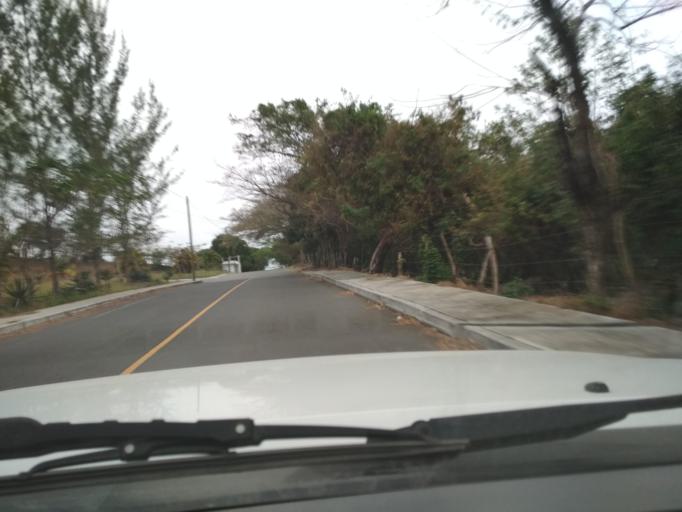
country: MX
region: Veracruz
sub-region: Medellin
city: Fraccionamiento Arboledas San Ramon
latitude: 19.0839
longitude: -96.1366
